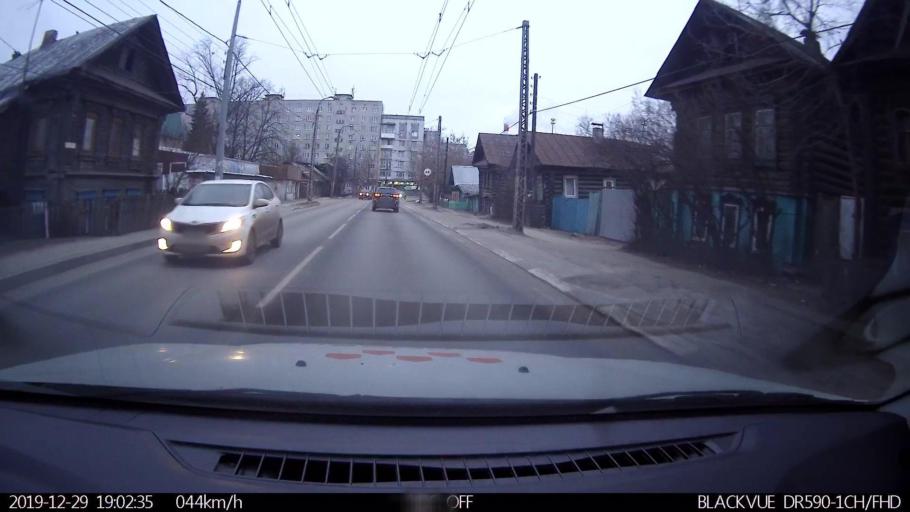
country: RU
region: Nizjnij Novgorod
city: Neklyudovo
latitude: 56.3616
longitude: 43.8622
